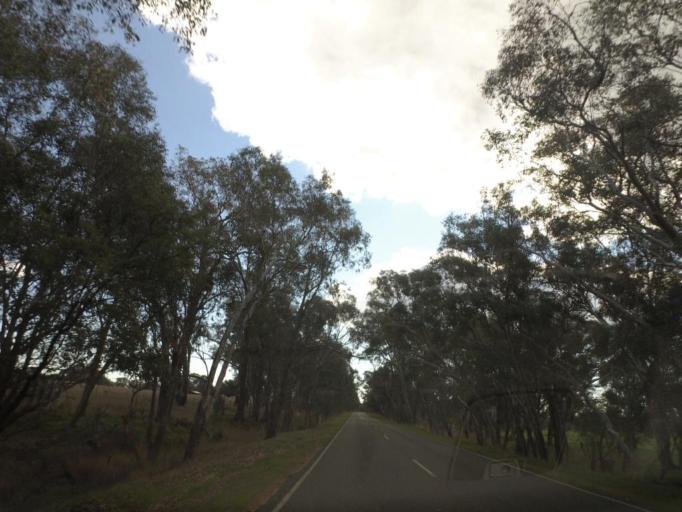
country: AU
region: New South Wales
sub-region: Corowa Shire
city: Howlong
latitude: -36.1865
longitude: 146.6101
